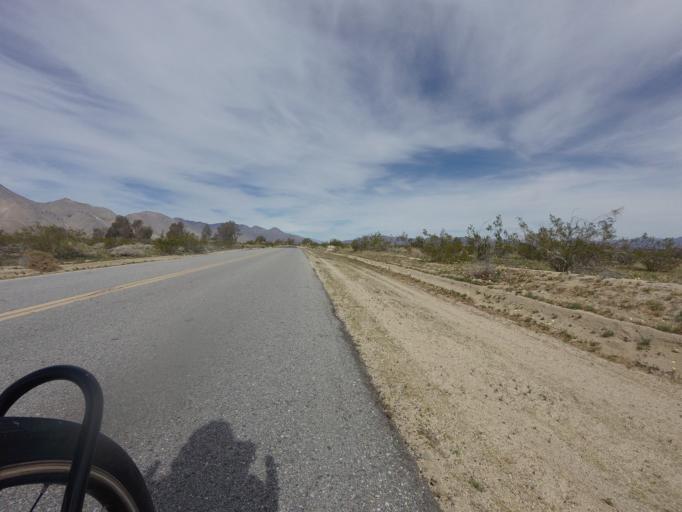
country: US
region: California
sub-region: Kern County
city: Inyokern
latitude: 35.7715
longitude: -117.8494
